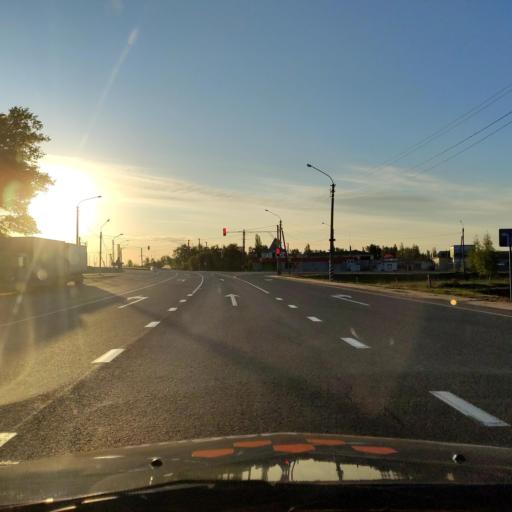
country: RU
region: Orjol
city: Livny
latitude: 52.4412
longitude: 37.5749
